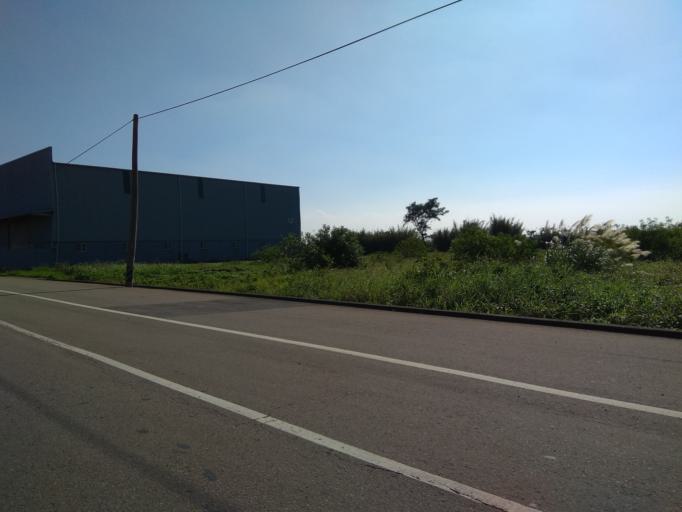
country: TW
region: Taiwan
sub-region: Hsinchu
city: Zhubei
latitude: 25.0287
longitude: 121.0778
